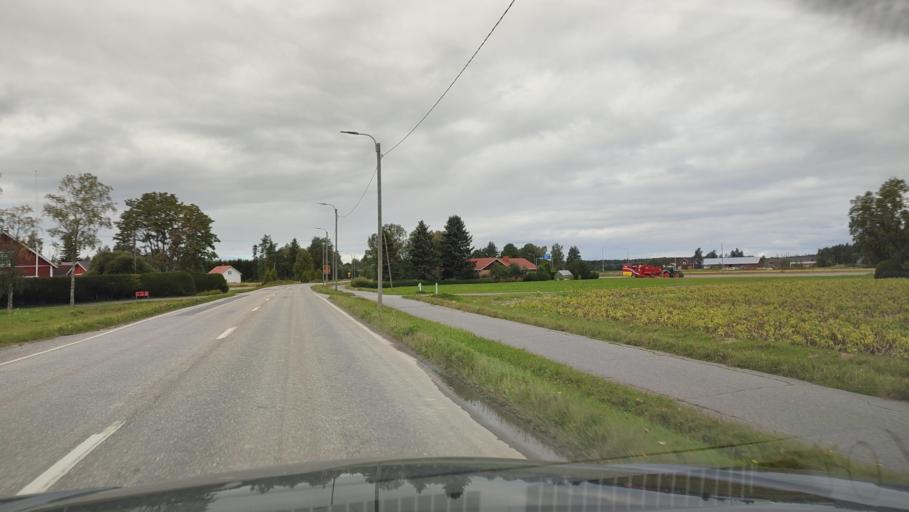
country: FI
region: Ostrobothnia
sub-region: Sydosterbotten
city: Kristinestad
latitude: 62.2581
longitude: 21.4944
